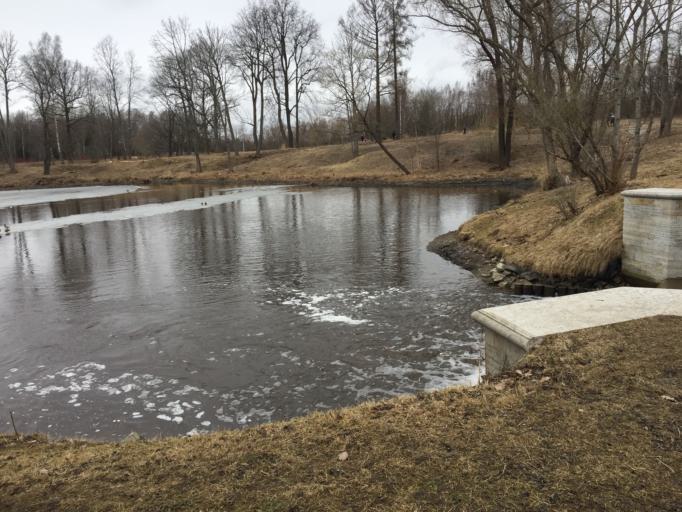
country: RU
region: St.-Petersburg
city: Pushkin
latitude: 59.7236
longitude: 30.3710
